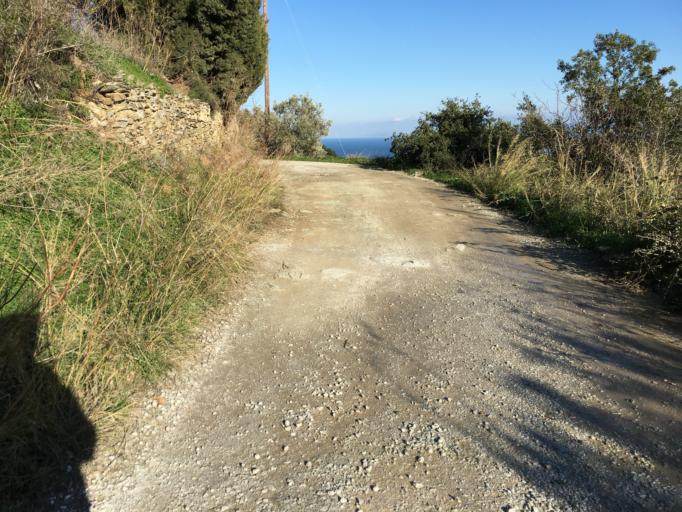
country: GR
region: Thessaly
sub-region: Nomos Magnisias
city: Skopelos
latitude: 39.1792
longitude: 23.6251
